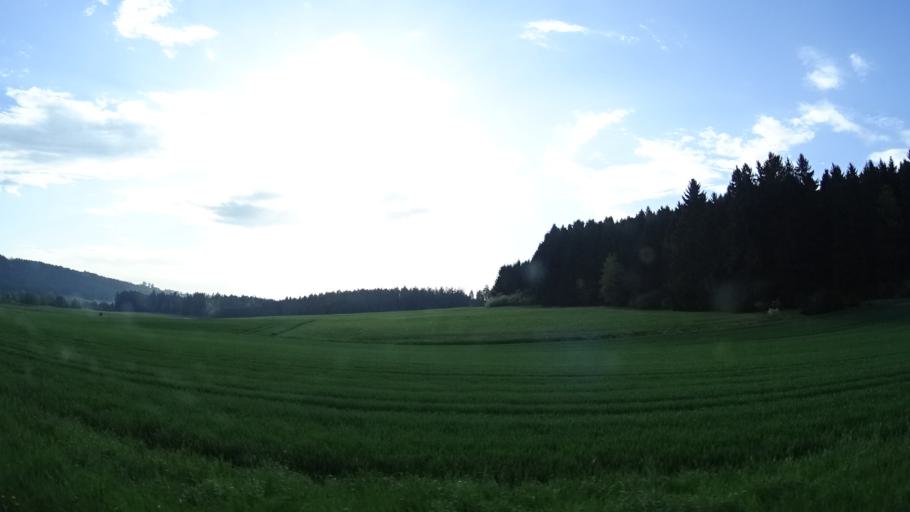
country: DE
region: Baden-Wuerttemberg
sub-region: Freiburg Region
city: Dietingen
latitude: 48.2259
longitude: 8.6587
